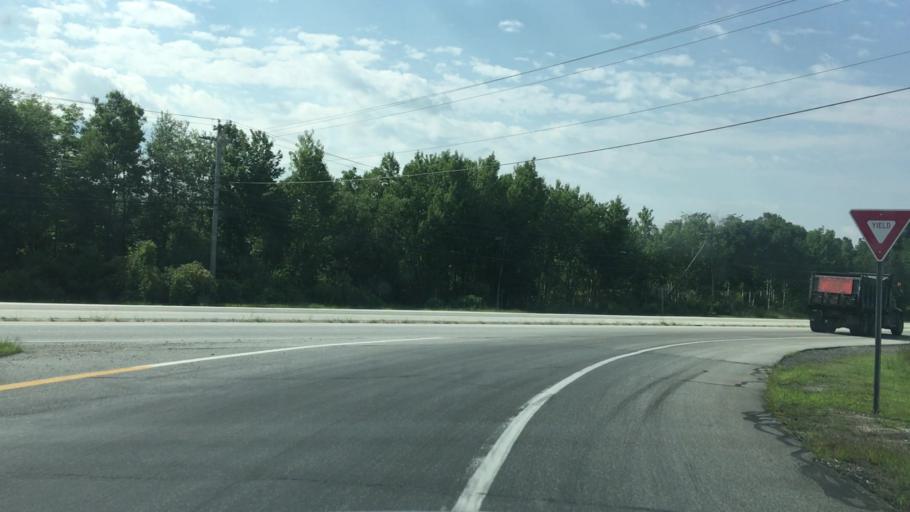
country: US
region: Maine
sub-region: Androscoggin County
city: Auburn
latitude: 44.0359
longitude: -70.2659
